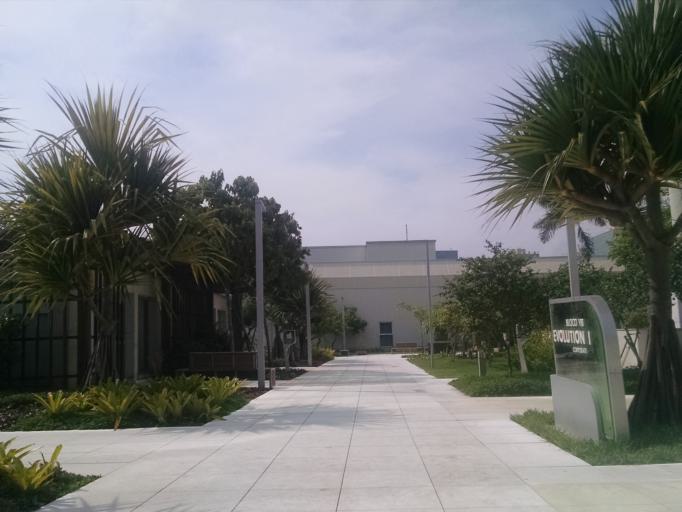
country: BR
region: Rio de Janeiro
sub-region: Rio De Janeiro
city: Rio de Janeiro
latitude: -22.9898
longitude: -43.3596
